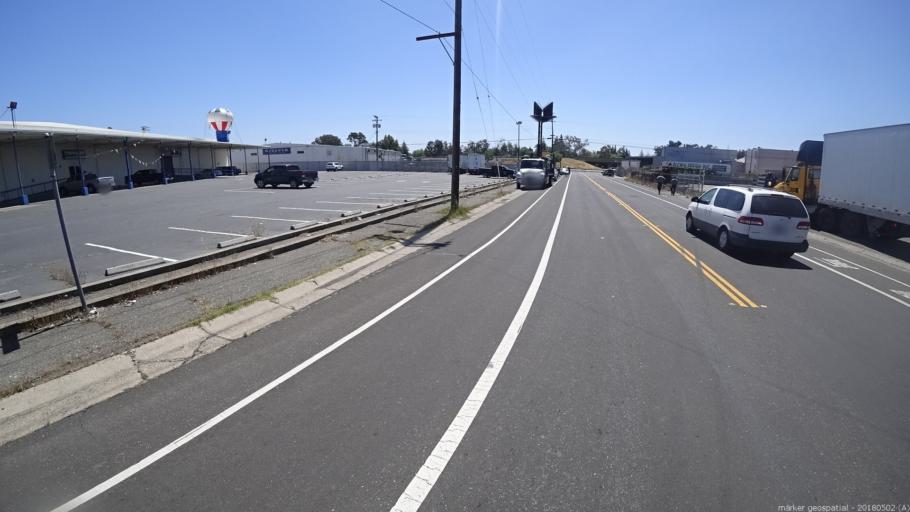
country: US
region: California
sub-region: Sacramento County
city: Sacramento
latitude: 38.6020
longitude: -121.4407
